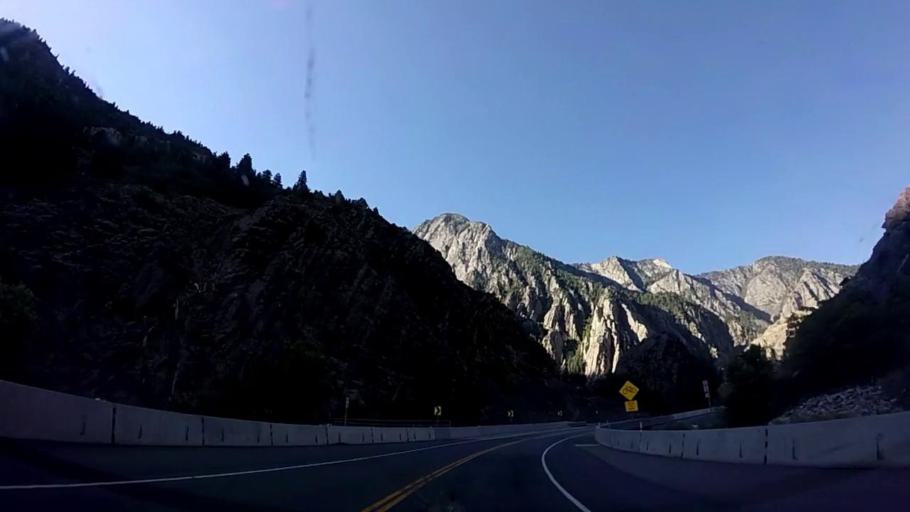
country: US
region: Utah
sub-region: Salt Lake County
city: Cottonwood Heights
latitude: 40.6265
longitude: -111.7421
